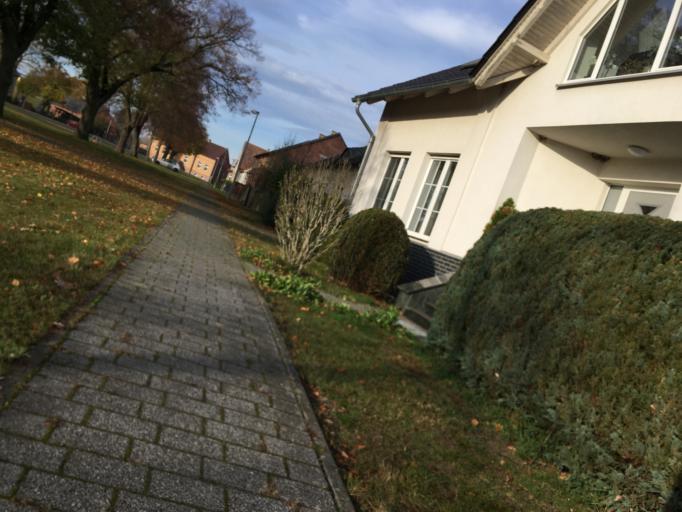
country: DE
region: Brandenburg
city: Luebben
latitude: 51.9721
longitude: 13.8857
